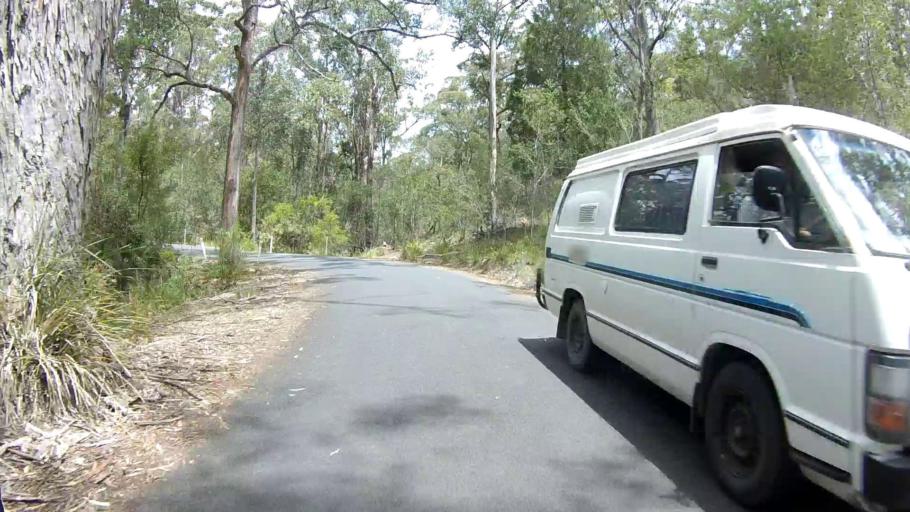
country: AU
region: Tasmania
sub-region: Sorell
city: Sorell
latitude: -42.5945
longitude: 147.9152
